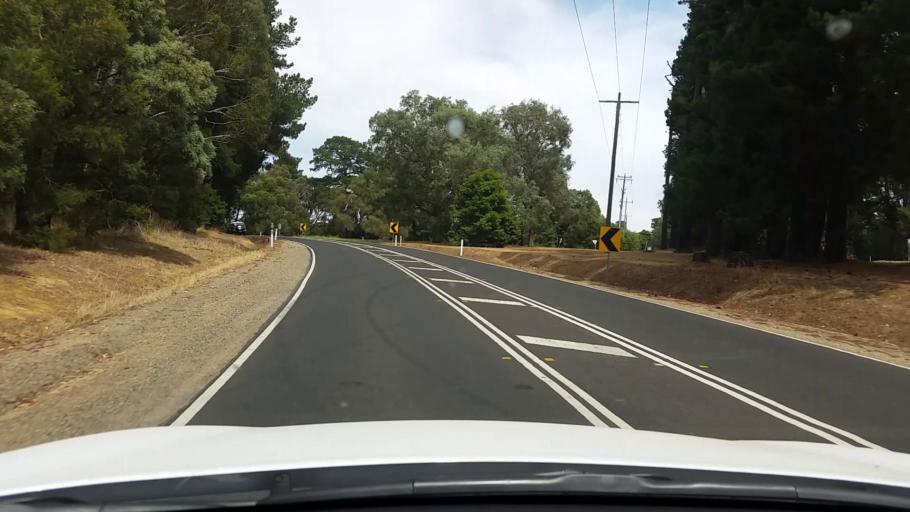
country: AU
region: Victoria
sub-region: Mornington Peninsula
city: Balnarring
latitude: -38.3742
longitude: 145.1137
